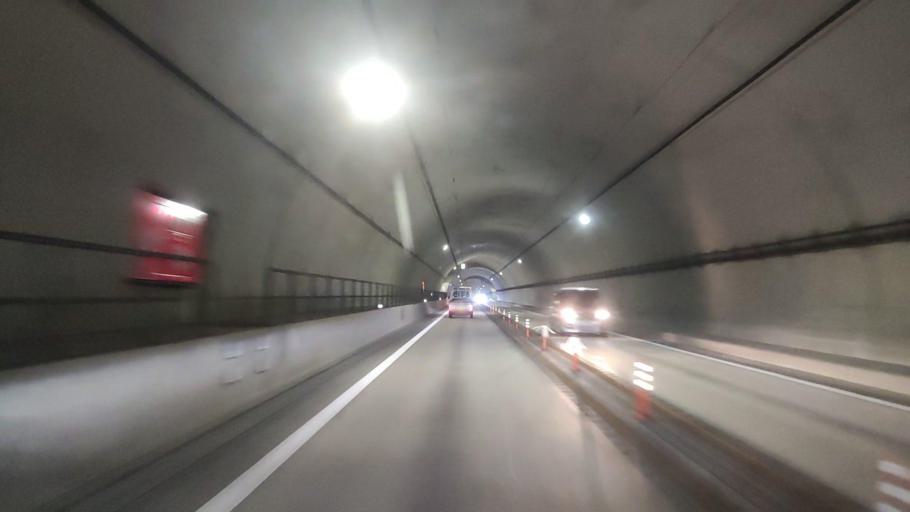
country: JP
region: Wakayama
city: Tanabe
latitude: 33.6034
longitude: 135.4304
